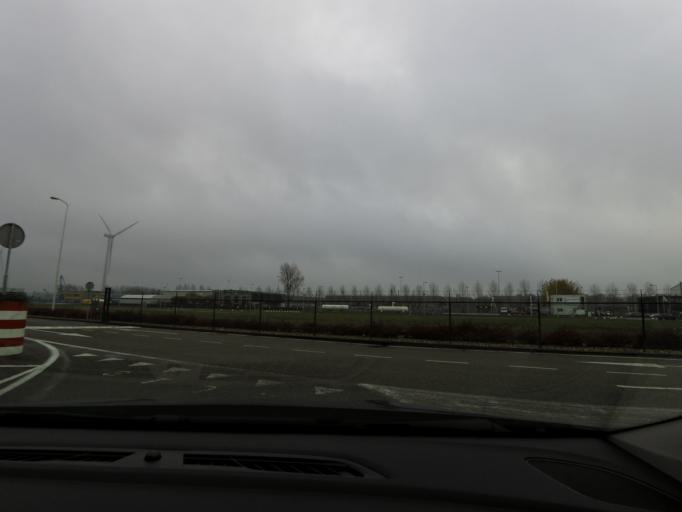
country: NL
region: South Holland
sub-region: Gemeente Brielle
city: Brielle
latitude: 51.9183
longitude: 4.1851
